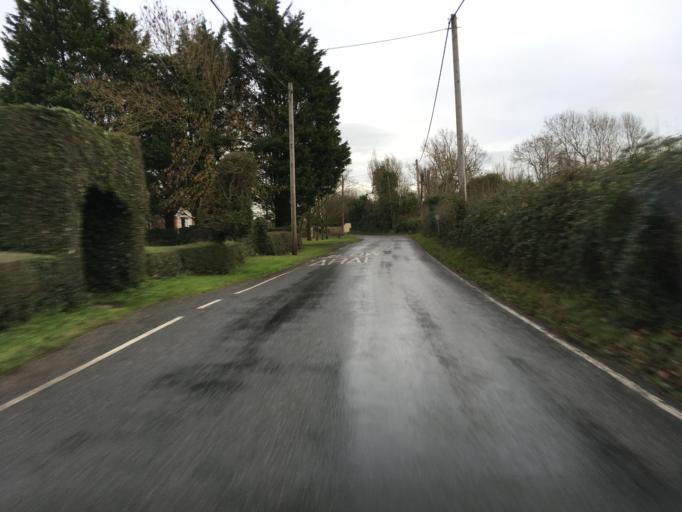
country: GB
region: Wales
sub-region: Newport
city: Goldcliff
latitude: 51.5425
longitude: -2.9117
